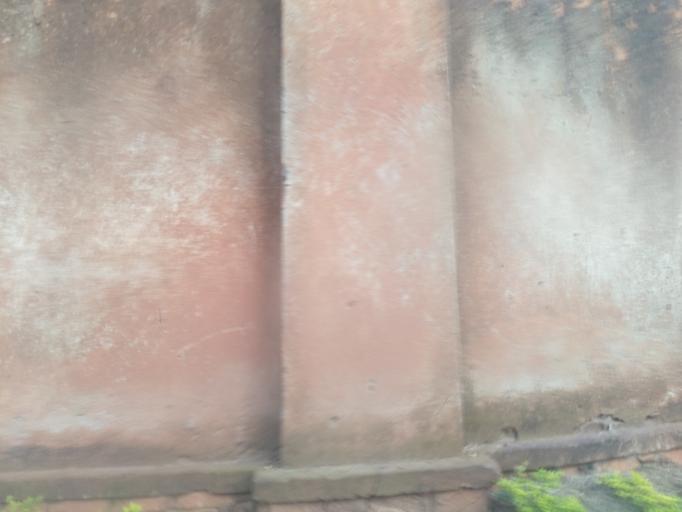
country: UG
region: Central Region
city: Kampala Central Division
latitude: 0.3491
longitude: 32.5937
